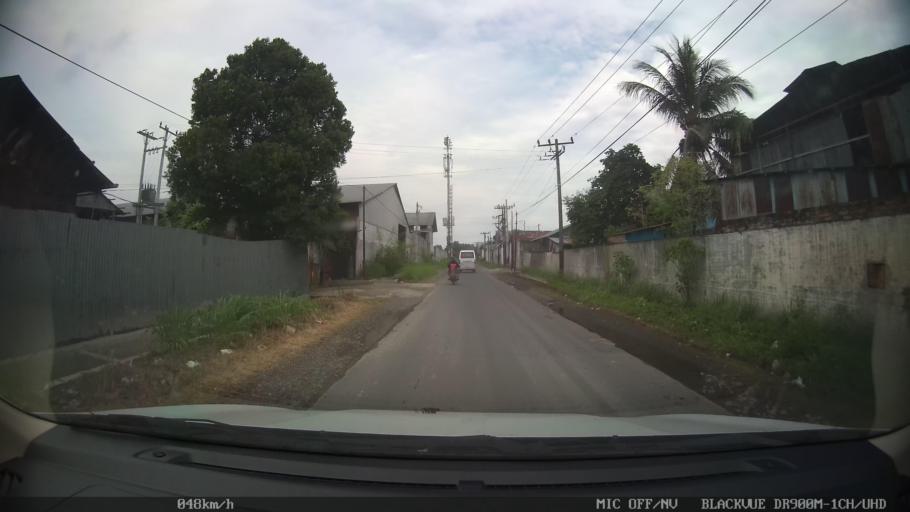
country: ID
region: North Sumatra
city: Sunggal
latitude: 3.6144
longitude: 98.5882
